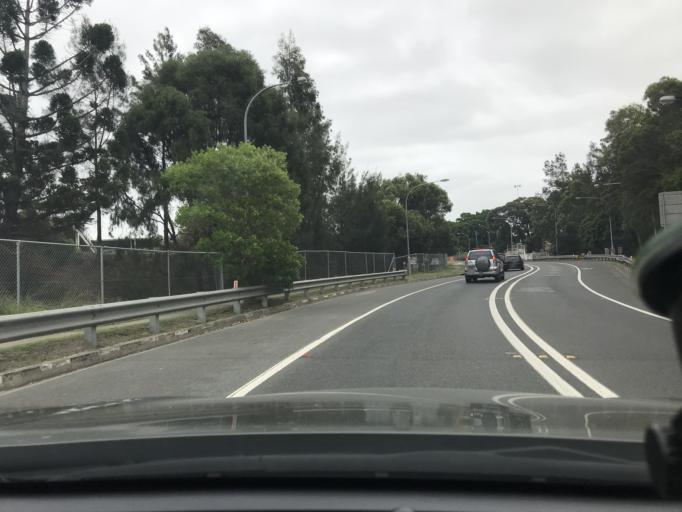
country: AU
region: New South Wales
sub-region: Ashfield
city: Croydon
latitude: -33.8681
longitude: 151.1117
